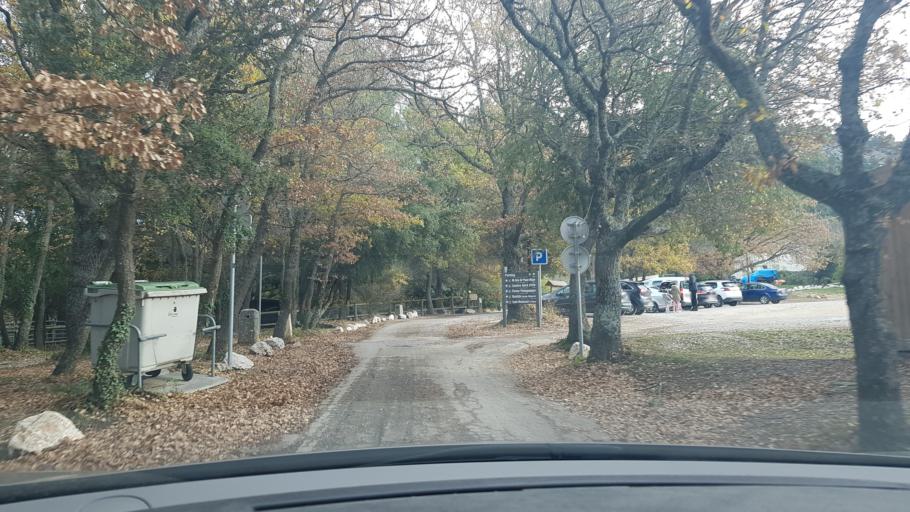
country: FR
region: Provence-Alpes-Cote d'Azur
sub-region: Departement des Bouches-du-Rhone
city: Mimet
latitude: 43.4135
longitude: 5.4718
